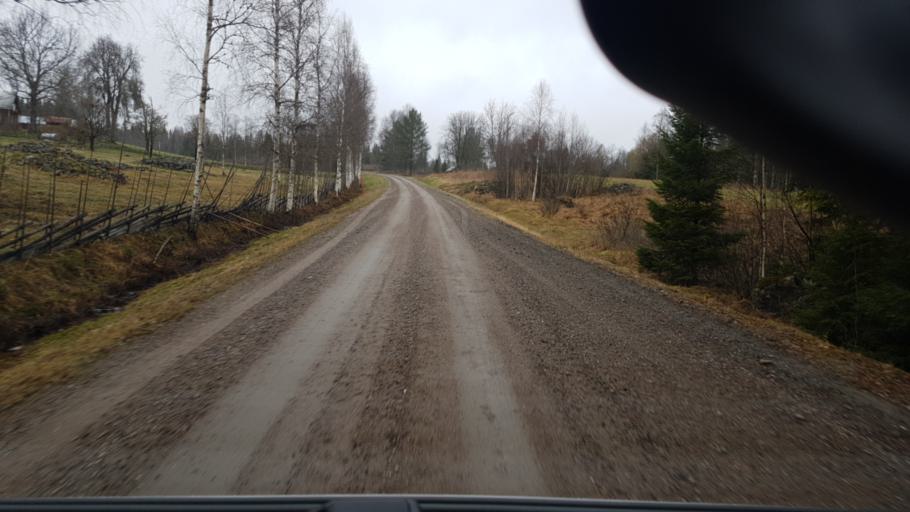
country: SE
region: Vaermland
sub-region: Eda Kommun
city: Charlottenberg
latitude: 59.9938
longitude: 12.5073
